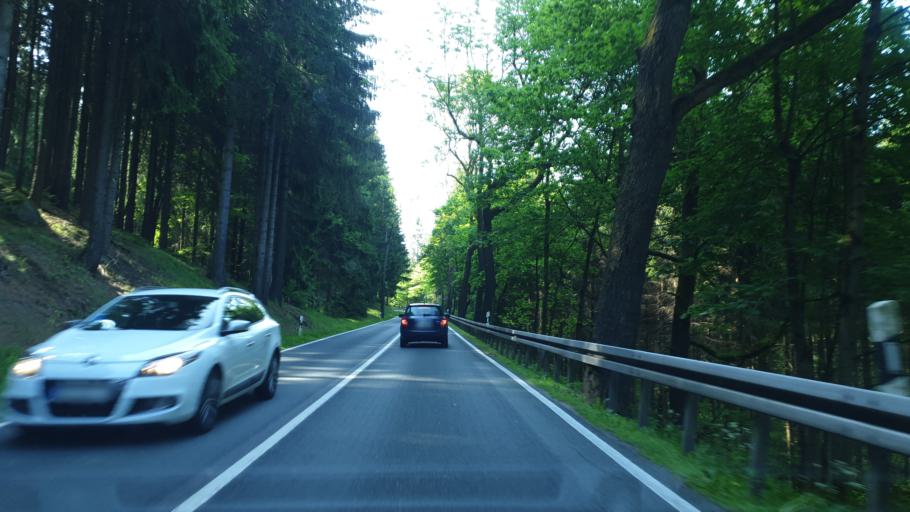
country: DE
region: Saxony
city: Eibenstock
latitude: 50.5133
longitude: 12.6080
